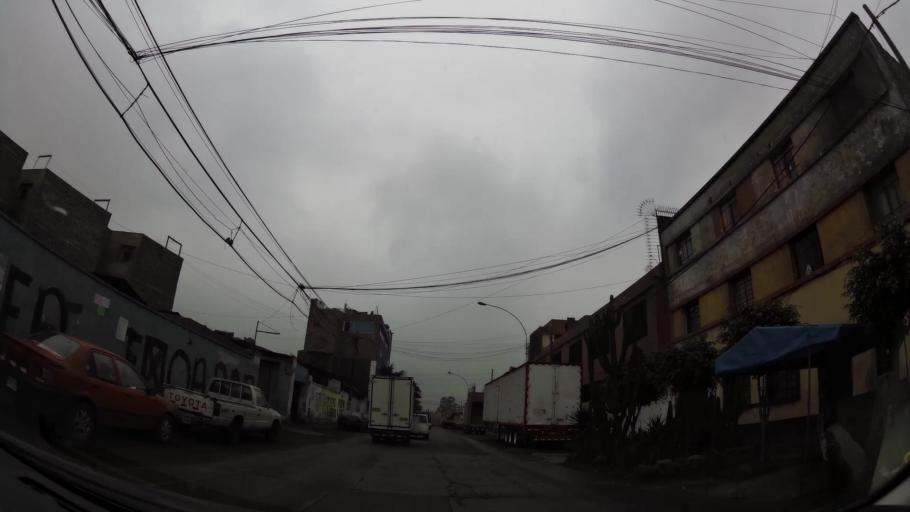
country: PE
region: Lima
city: Lima
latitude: -12.0664
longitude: -77.0258
